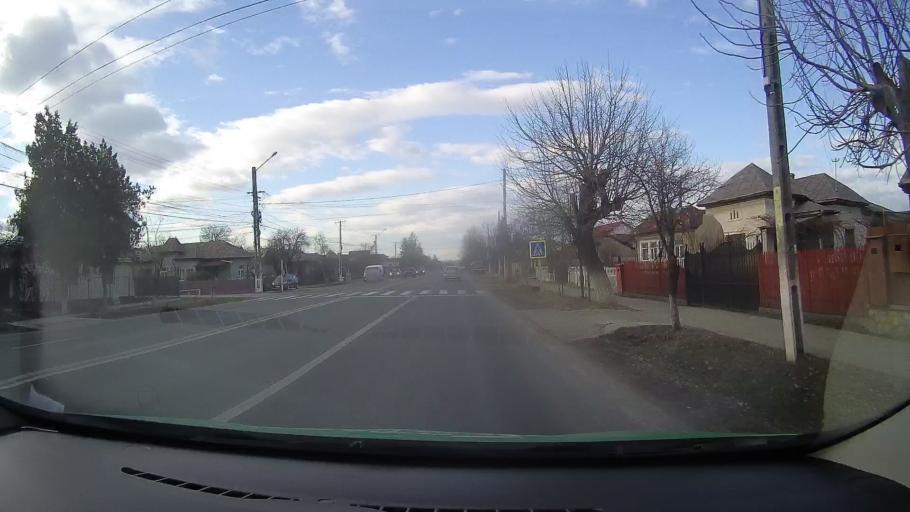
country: RO
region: Dambovita
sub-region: Comuna Ulmi
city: Ulmi
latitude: 44.8977
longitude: 25.4993
